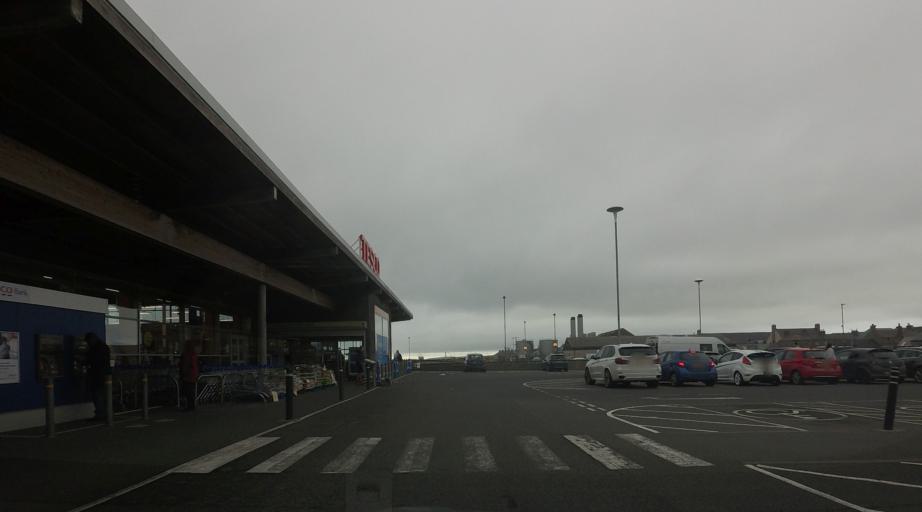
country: GB
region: Scotland
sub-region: Orkney Islands
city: Orkney
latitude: 58.9805
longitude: -2.9671
